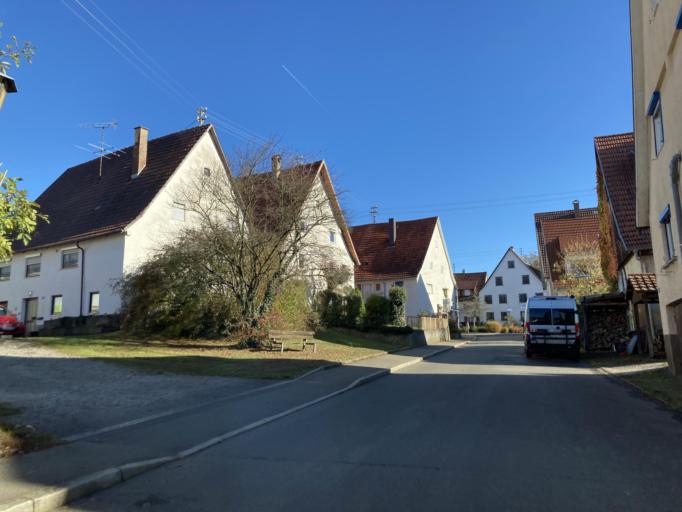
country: DE
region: Baden-Wuerttemberg
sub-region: Tuebingen Region
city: Mossingen
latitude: 48.3946
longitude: 9.0400
